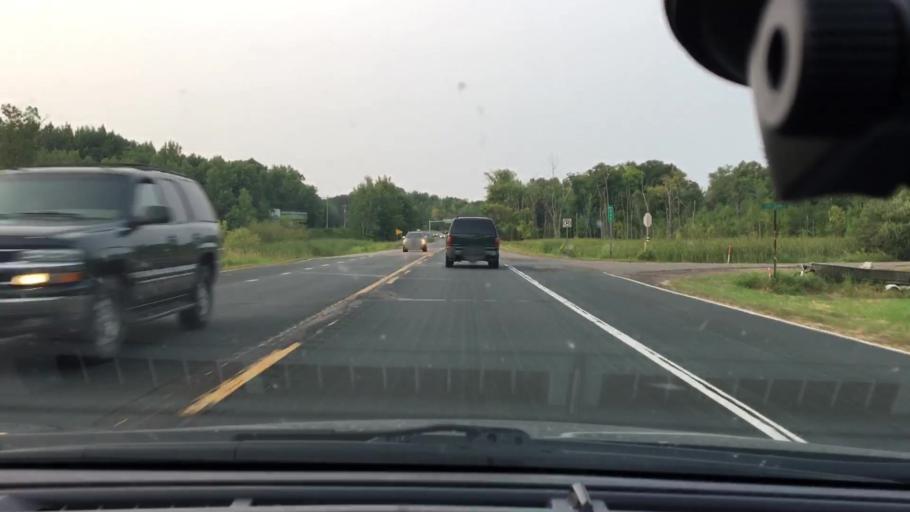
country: US
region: Minnesota
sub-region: Mille Lacs County
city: Vineland
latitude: 46.2186
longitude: -93.7925
